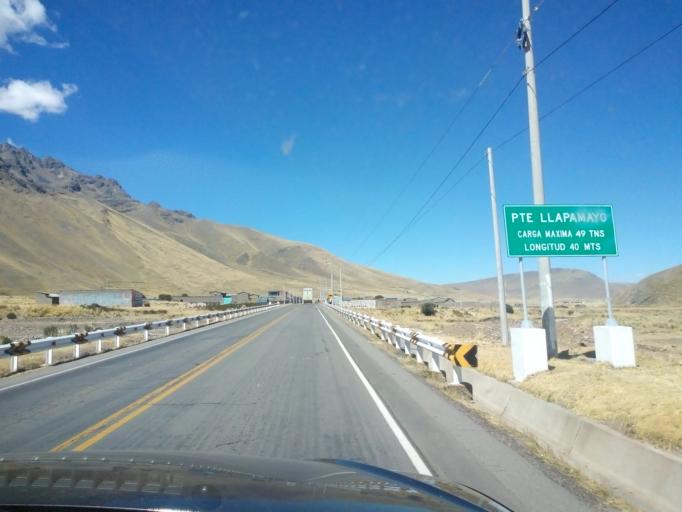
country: PE
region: Puno
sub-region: Provincia de Melgar
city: Santa Rosa
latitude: -14.5343
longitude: -70.8875
